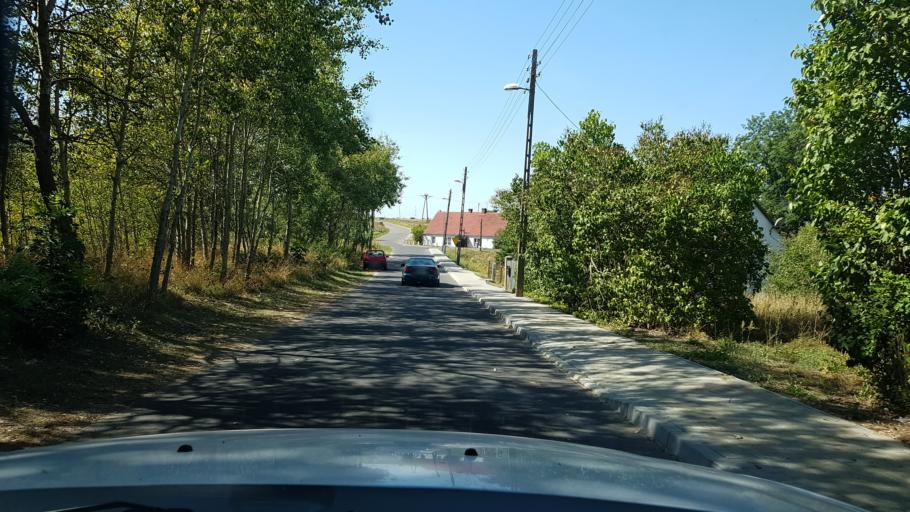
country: PL
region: West Pomeranian Voivodeship
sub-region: Powiat gryfinski
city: Moryn
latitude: 52.8487
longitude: 14.3936
